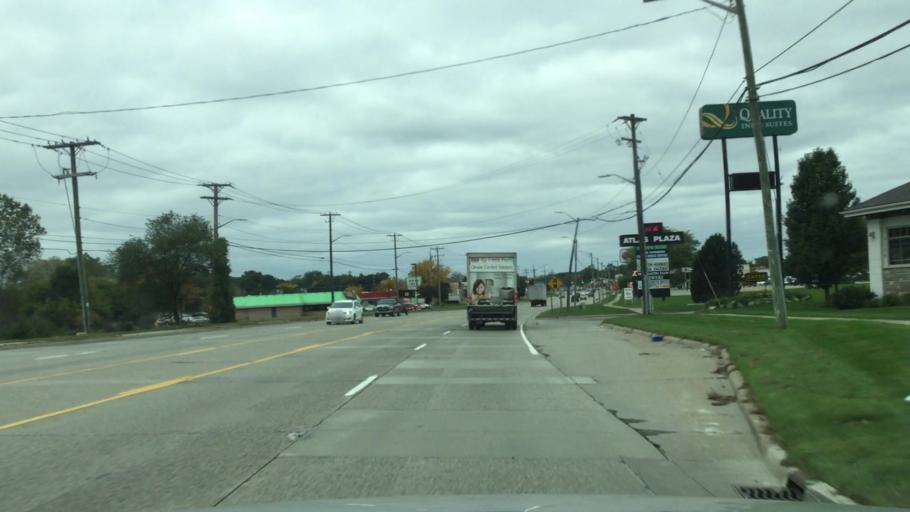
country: US
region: Michigan
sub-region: Oakland County
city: Waterford
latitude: 42.6595
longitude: -83.4267
